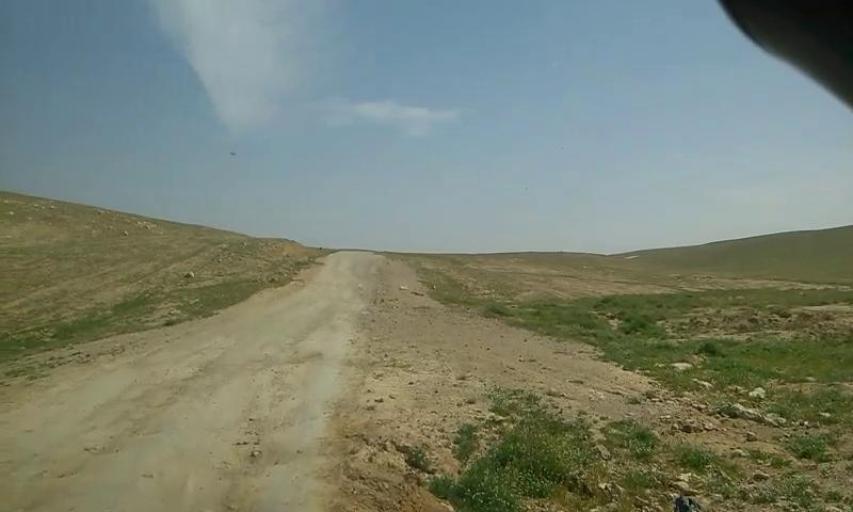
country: PS
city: `Arab ar Rashaydah
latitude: 31.5277
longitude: 35.2930
